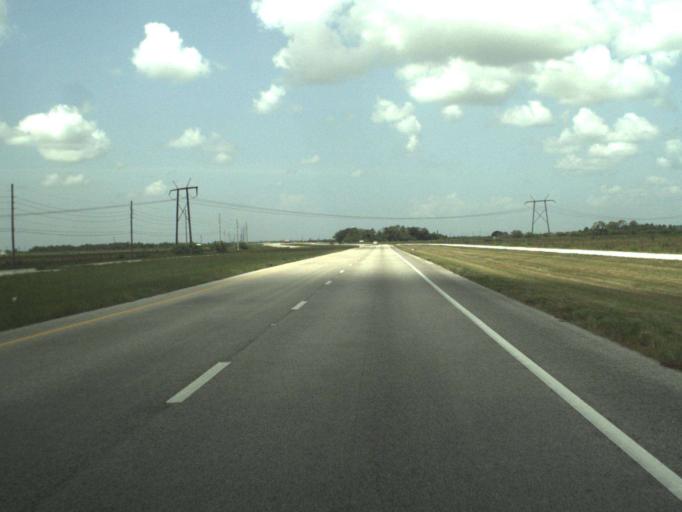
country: US
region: Florida
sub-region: Saint Lucie County
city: Fort Pierce South
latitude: 27.3862
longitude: -80.4657
